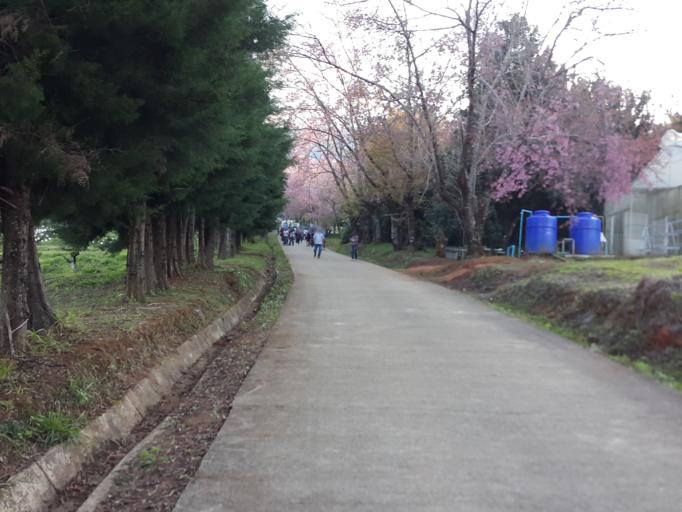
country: TH
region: Chiang Mai
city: Mae Chaem
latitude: 18.6316
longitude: 98.5047
